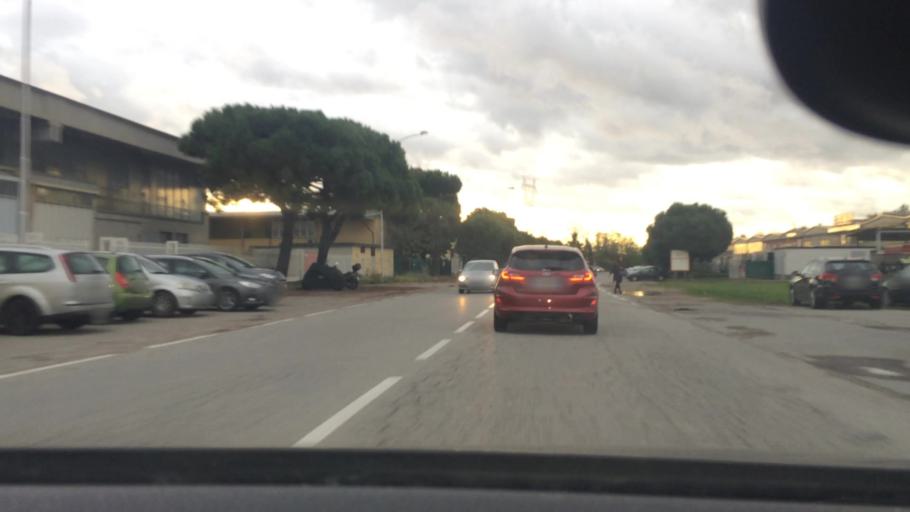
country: IT
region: Lombardy
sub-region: Citta metropolitana di Milano
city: Nerviano
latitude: 45.5432
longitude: 8.9673
